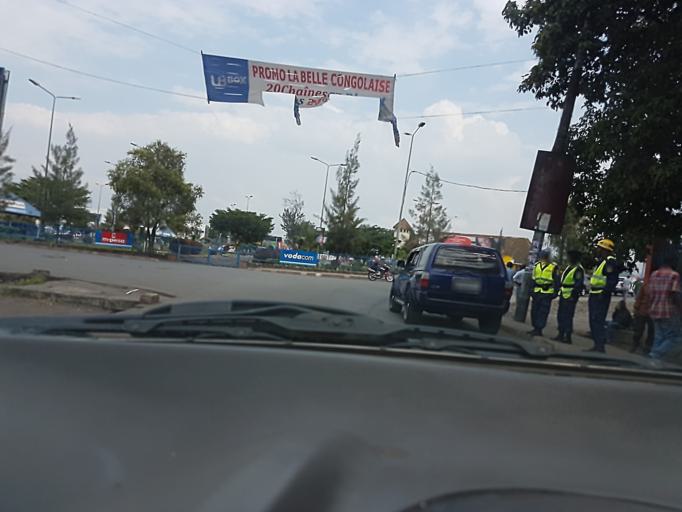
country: CD
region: Nord Kivu
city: Goma
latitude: -1.6892
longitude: 29.2374
